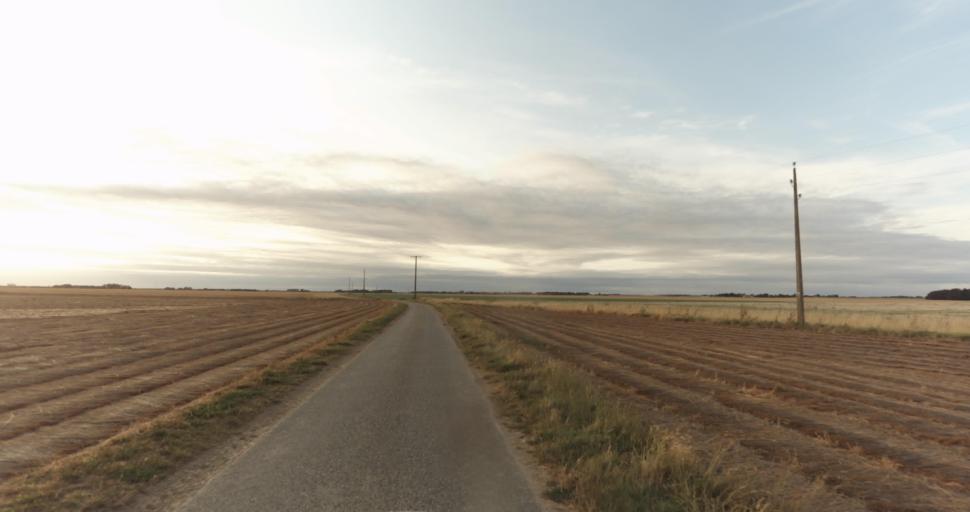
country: FR
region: Haute-Normandie
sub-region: Departement de l'Eure
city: La Madeleine-de-Nonancourt
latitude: 48.8562
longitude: 1.2124
